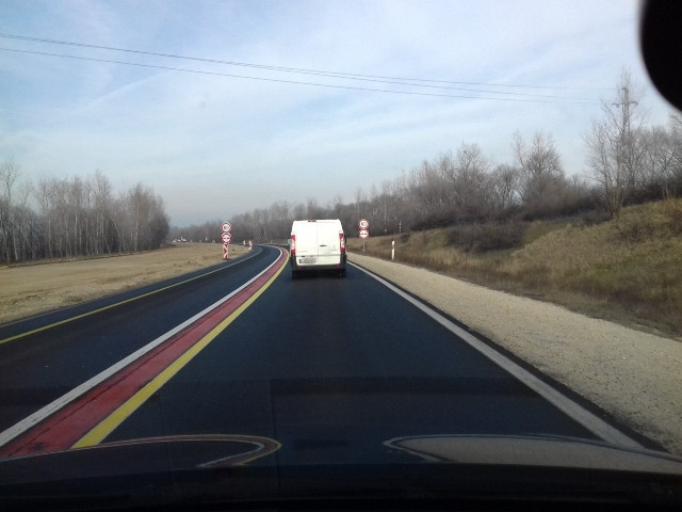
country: HU
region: Pest
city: Fot
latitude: 47.6368
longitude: 19.1696
